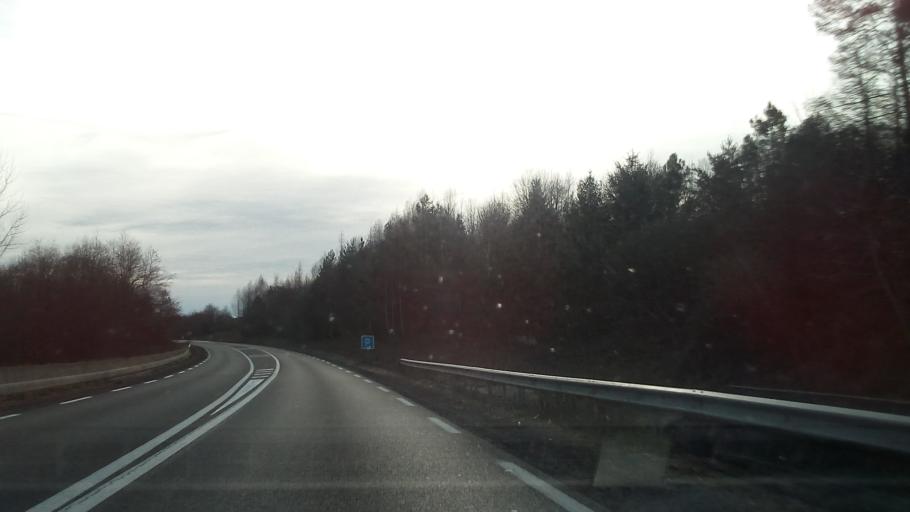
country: FR
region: Limousin
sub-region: Departement de la Correze
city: Seilhac
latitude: 45.3680
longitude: 1.6991
